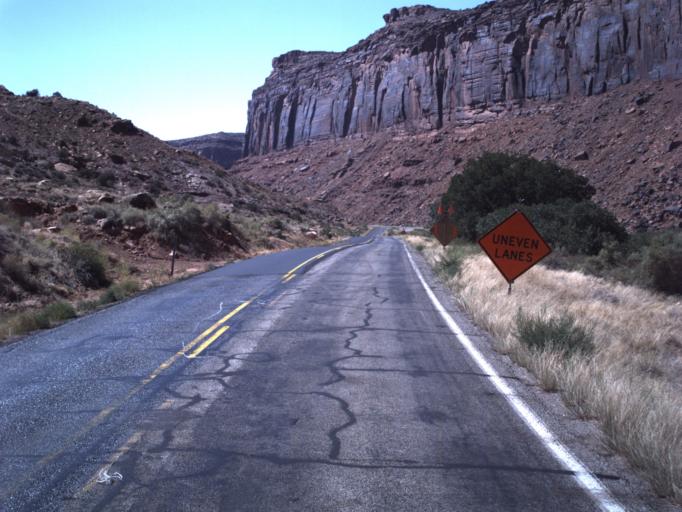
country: US
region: Utah
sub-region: Grand County
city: Moab
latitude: 38.6829
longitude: -109.4727
